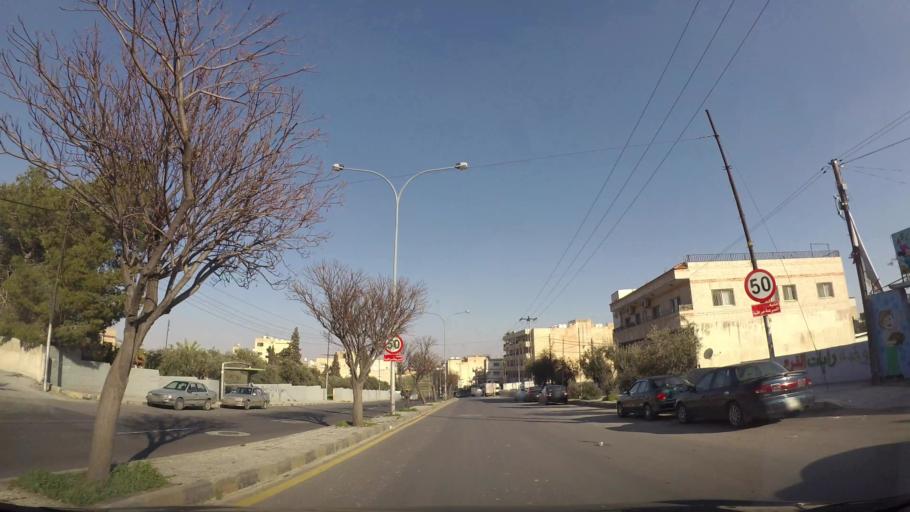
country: JO
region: Amman
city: Amman
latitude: 31.9741
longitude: 35.9659
